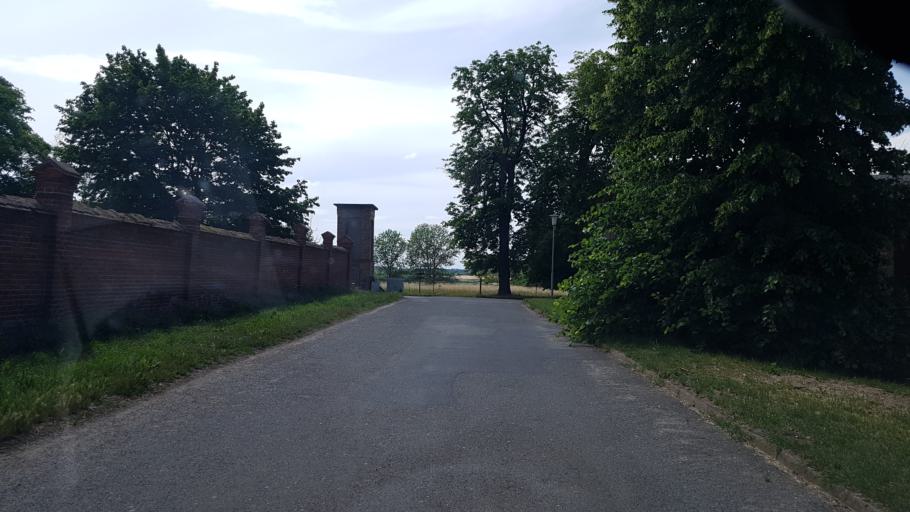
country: DE
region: Brandenburg
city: Prenzlau
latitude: 53.3849
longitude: 13.7704
